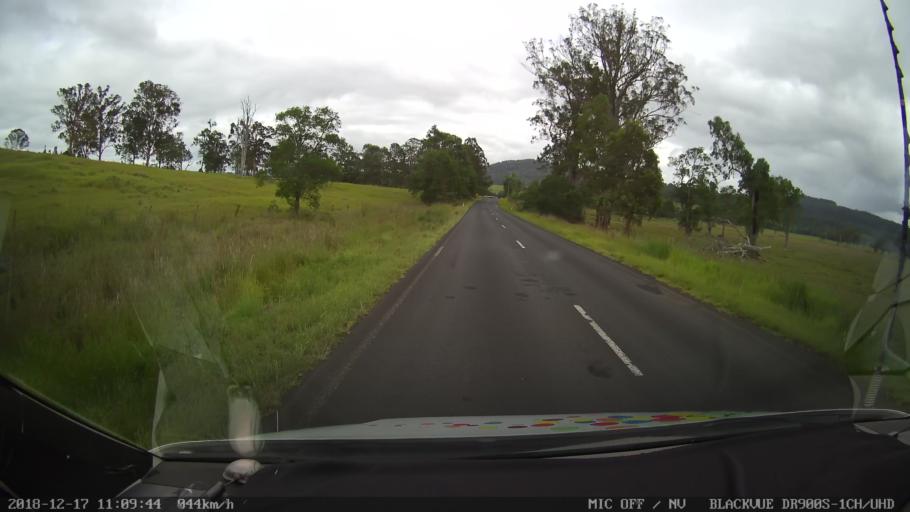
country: AU
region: New South Wales
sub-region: Kyogle
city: Kyogle
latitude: -28.7523
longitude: 152.6531
